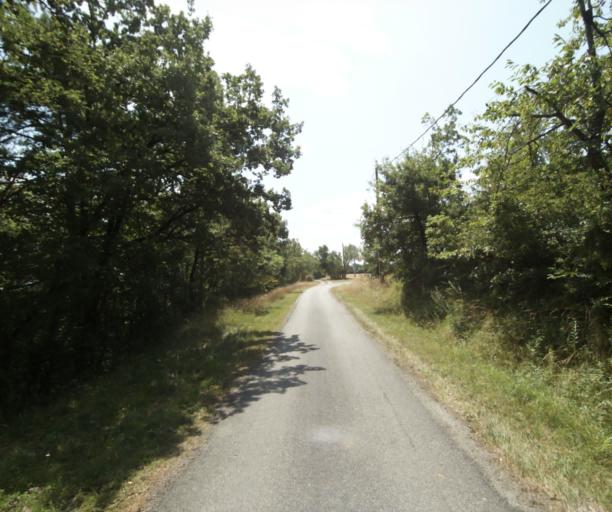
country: FR
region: Midi-Pyrenees
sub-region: Departement de la Haute-Garonne
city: Saint-Felix-Lauragais
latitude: 43.4351
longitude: 1.8833
